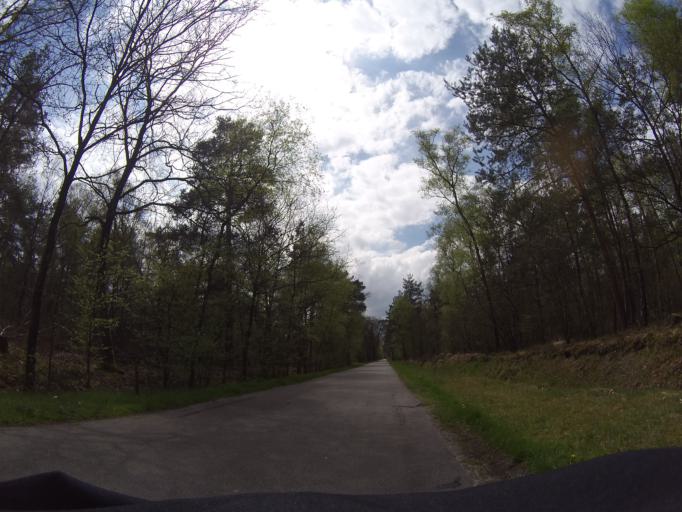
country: NL
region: Overijssel
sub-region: Gemeente Twenterand
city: Den Ham
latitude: 52.5173
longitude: 6.4853
